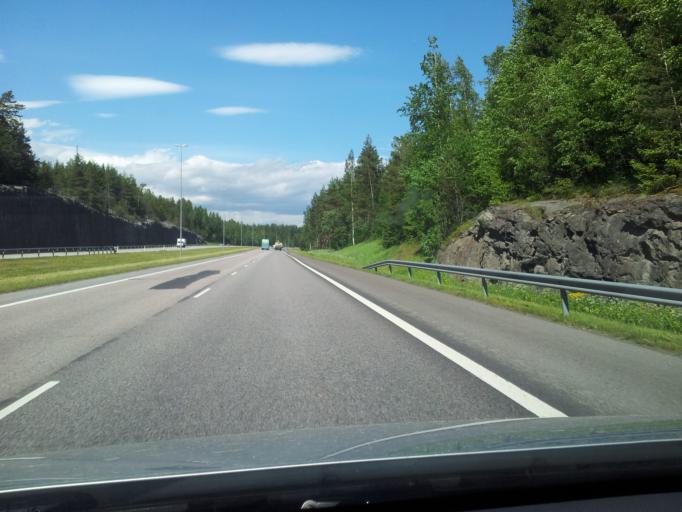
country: FI
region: Uusimaa
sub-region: Porvoo
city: Porvoo
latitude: 60.3470
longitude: 25.5148
